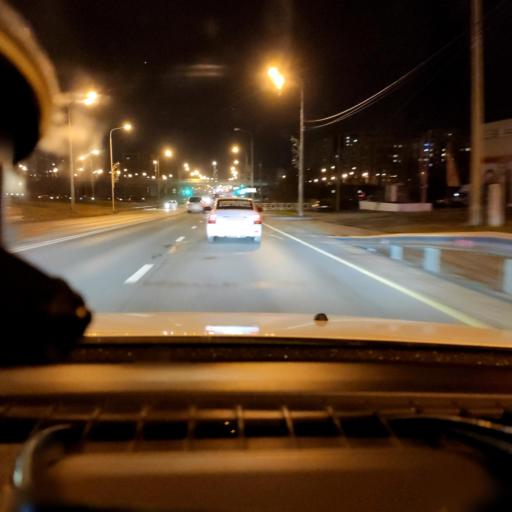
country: RU
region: Samara
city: Samara
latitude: 53.2711
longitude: 50.2236
